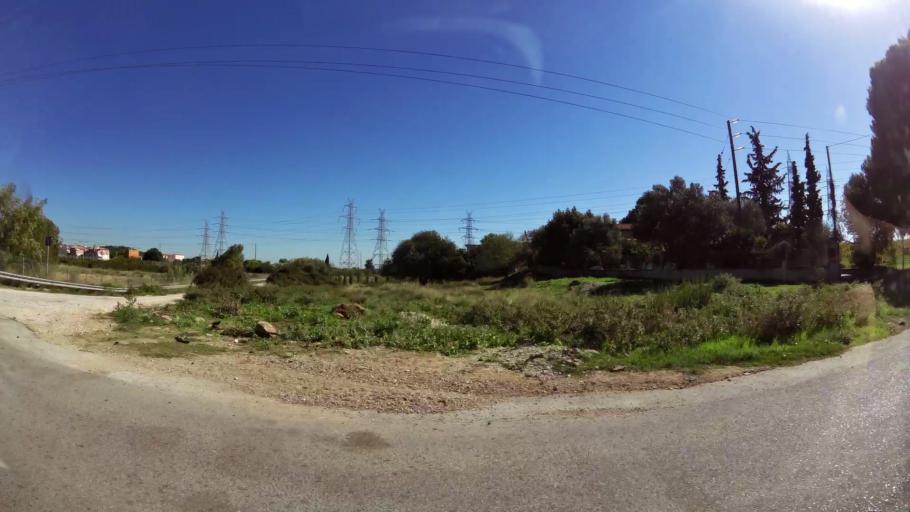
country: GR
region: Attica
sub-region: Nomarchia Anatolikis Attikis
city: Leondarion
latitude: 37.9962
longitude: 23.8568
